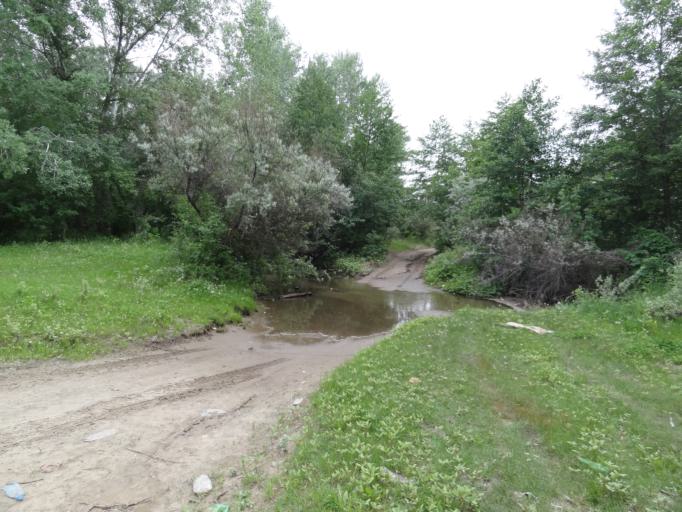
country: RU
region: Saratov
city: Privolzhskiy
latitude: 51.1906
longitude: 45.9159
